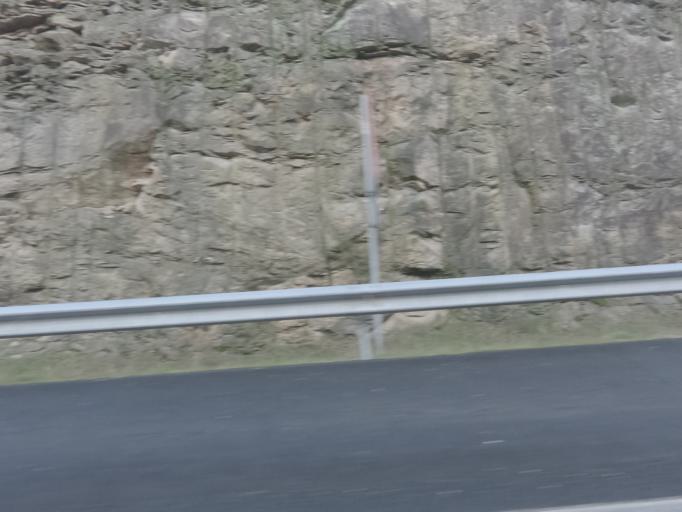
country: ES
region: Galicia
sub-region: Provincia da Coruna
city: Ribeira
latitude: 42.7397
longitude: -8.3699
